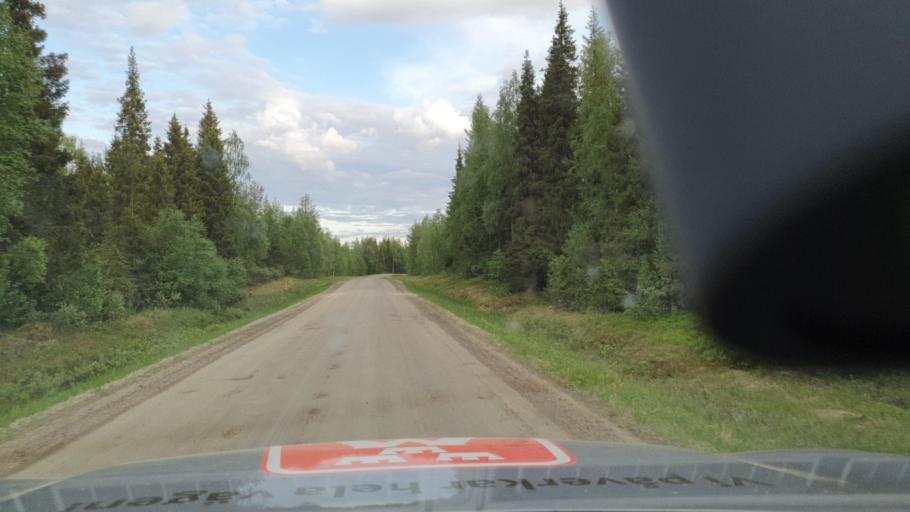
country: SE
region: Norrbotten
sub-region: Gallivare Kommun
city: Gaellivare
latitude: 66.7387
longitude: 21.1392
